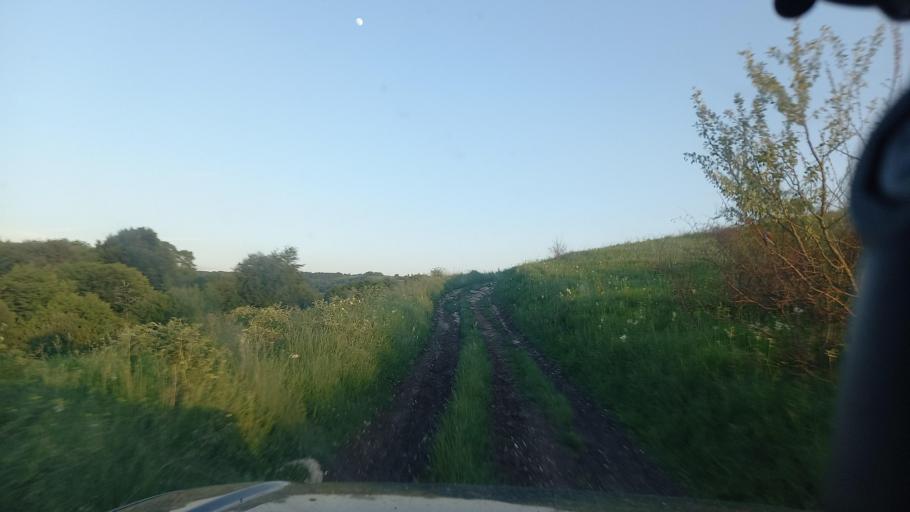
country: RU
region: Karachayevo-Cherkesiya
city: Pregradnaya
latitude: 44.1139
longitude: 41.1203
